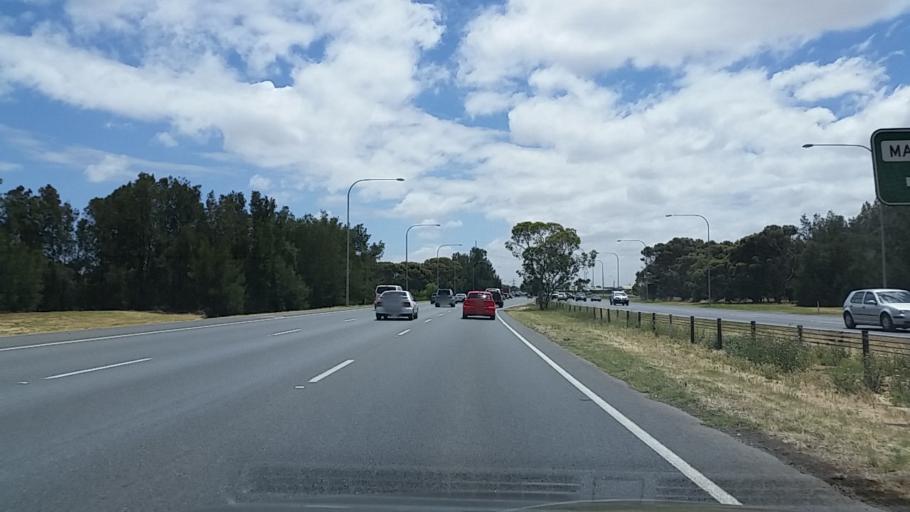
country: AU
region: South Australia
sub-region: Salisbury
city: Salisbury
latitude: -34.7978
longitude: 138.5963
